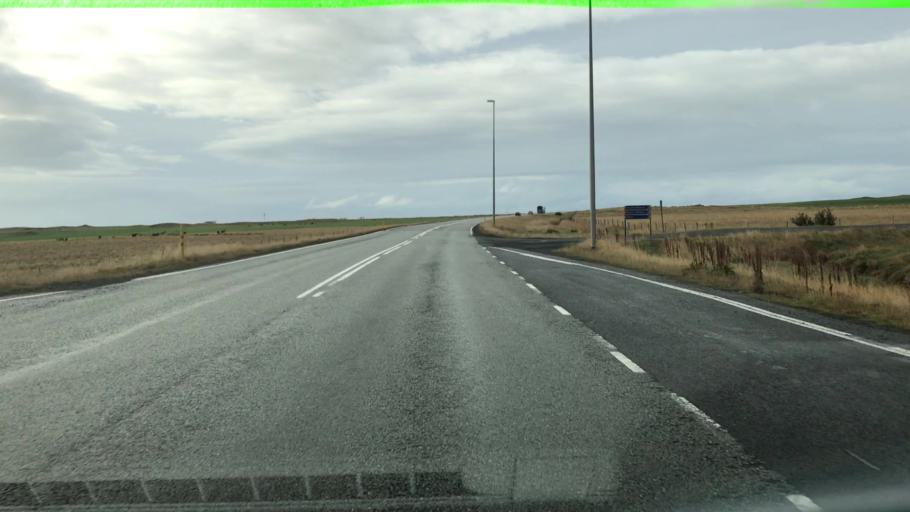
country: IS
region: West
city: Akranes
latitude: 64.3100
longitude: -21.9901
